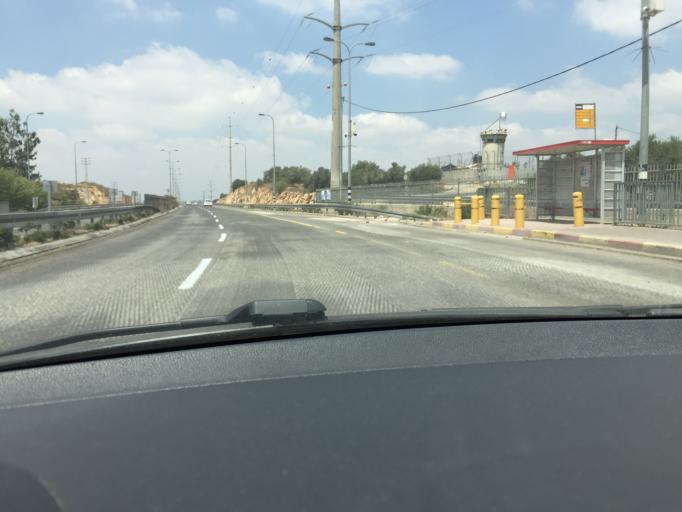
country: PS
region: West Bank
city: Kifil Haris
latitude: 32.1097
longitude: 35.1648
